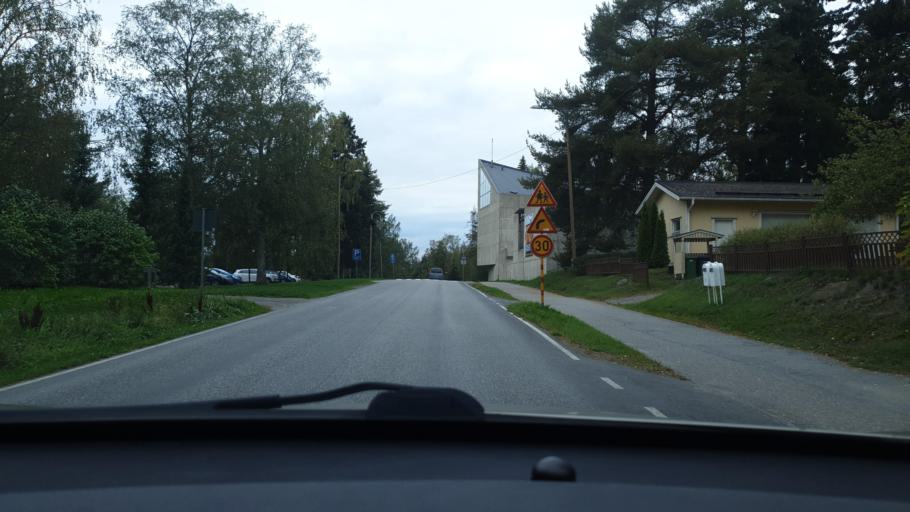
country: FI
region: Ostrobothnia
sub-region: Vaasa
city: Korsholm
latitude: 63.0957
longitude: 21.6648
